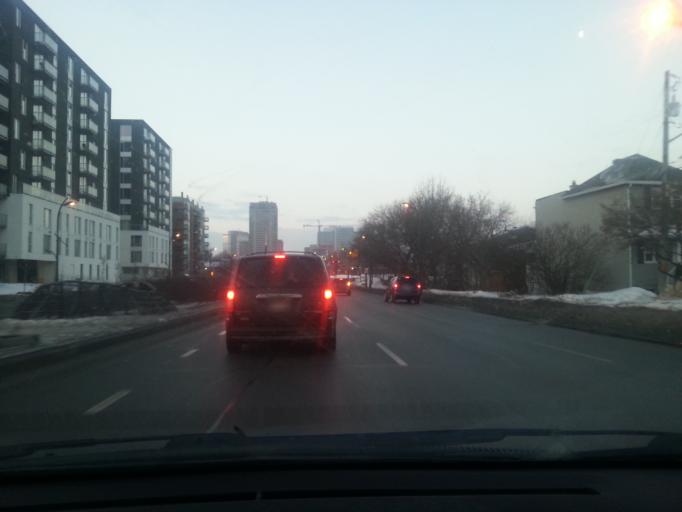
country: CA
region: Ontario
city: Ottawa
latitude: 45.4362
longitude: -75.7123
